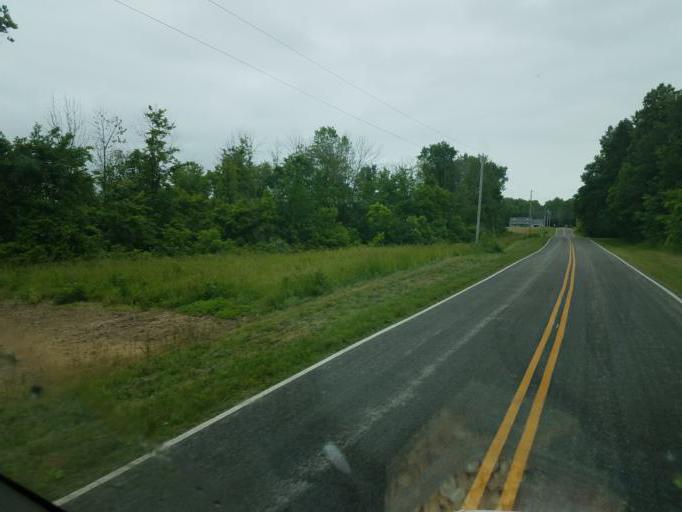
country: US
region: Ohio
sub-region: Marion County
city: Marion
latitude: 40.5501
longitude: -83.0176
